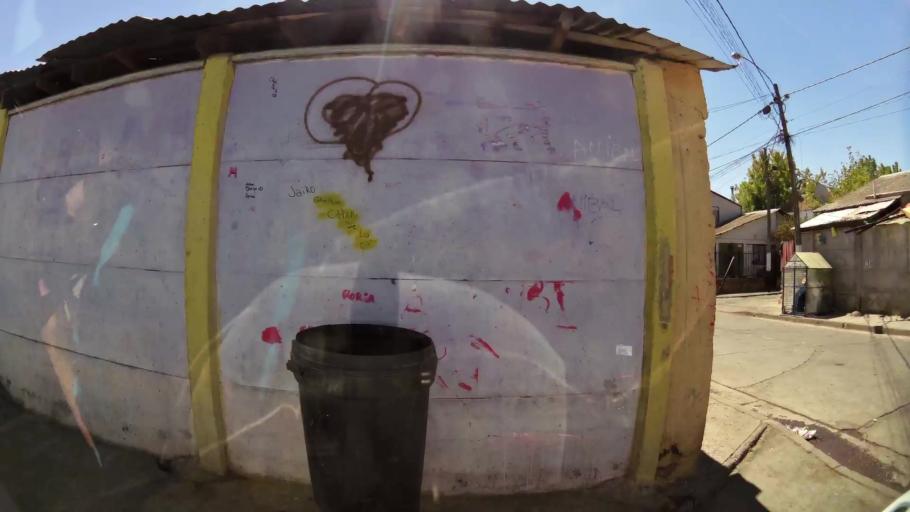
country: CL
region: O'Higgins
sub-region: Provincia de Colchagua
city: Chimbarongo
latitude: -34.5744
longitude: -70.9843
